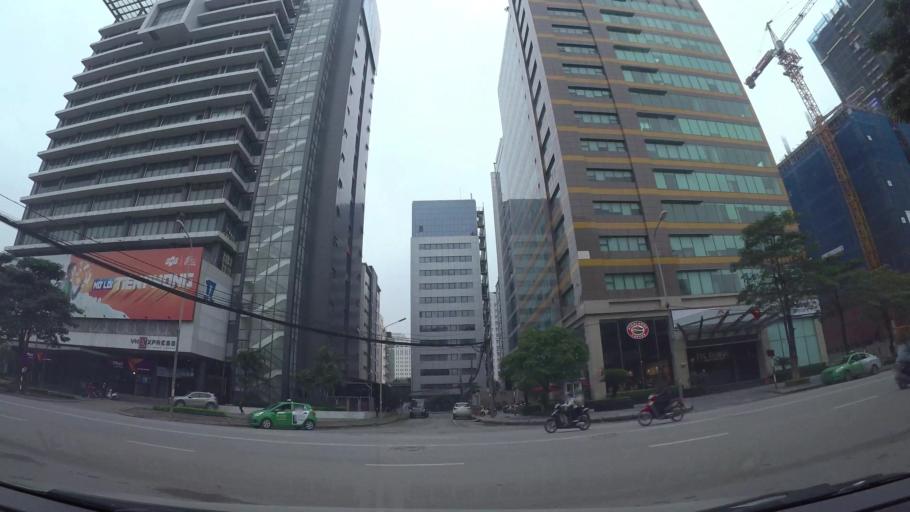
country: VN
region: Ha Noi
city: Cau Dien
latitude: 21.0314
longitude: 105.7824
